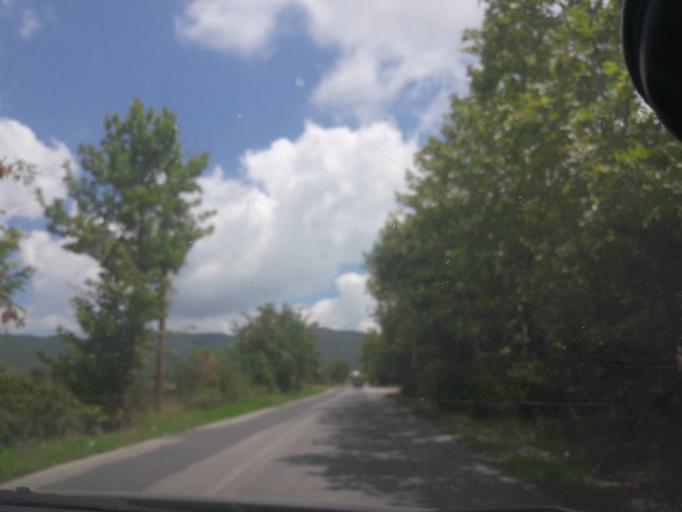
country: GR
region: Central Macedonia
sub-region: Nomos Chalkidikis
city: Polygyros
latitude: 40.3734
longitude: 23.4322
